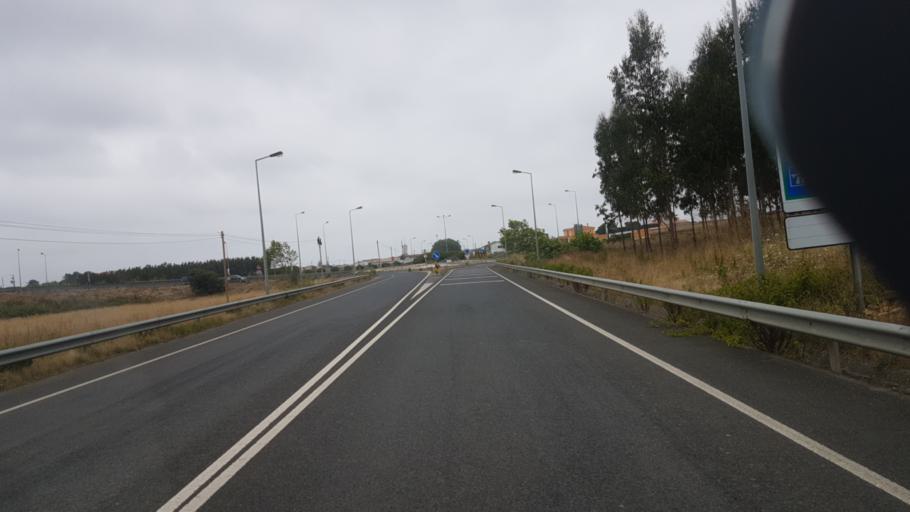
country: PT
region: Leiria
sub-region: Peniche
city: Atouguia da Baleia
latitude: 39.3329
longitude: -9.2558
